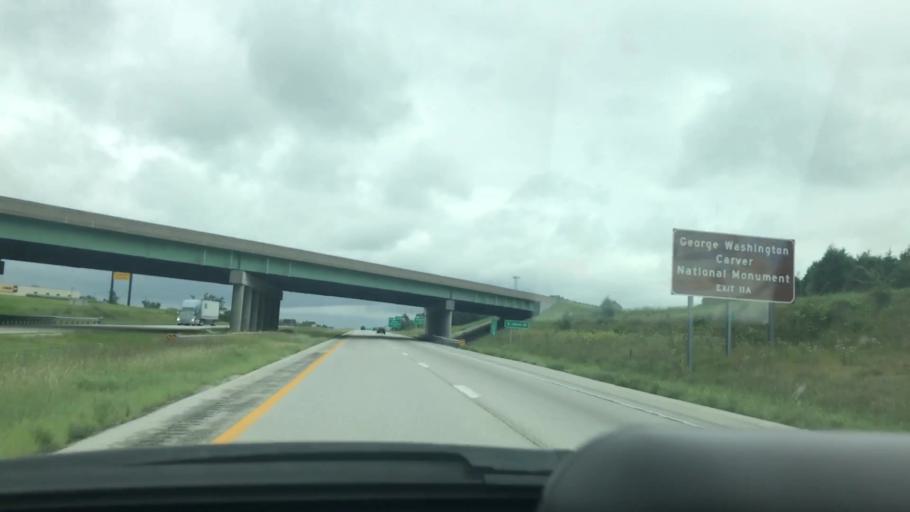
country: US
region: Missouri
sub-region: Jasper County
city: Duquesne
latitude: 37.0551
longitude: -94.4458
